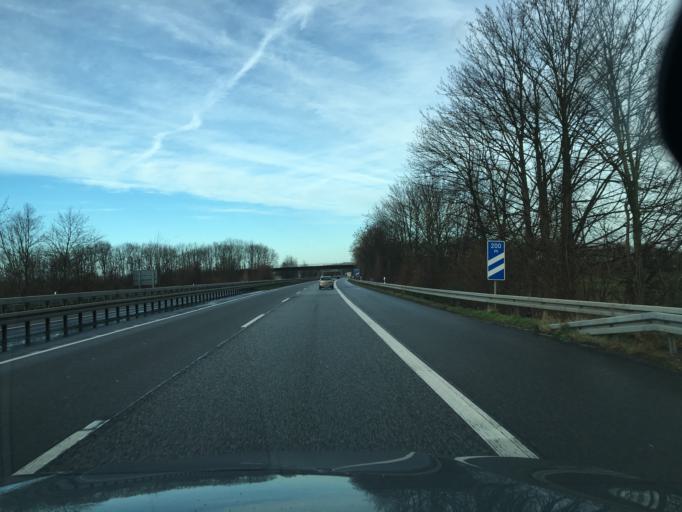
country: DE
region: North Rhine-Westphalia
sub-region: Regierungsbezirk Koln
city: Rheinbach
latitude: 50.6147
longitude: 6.9854
